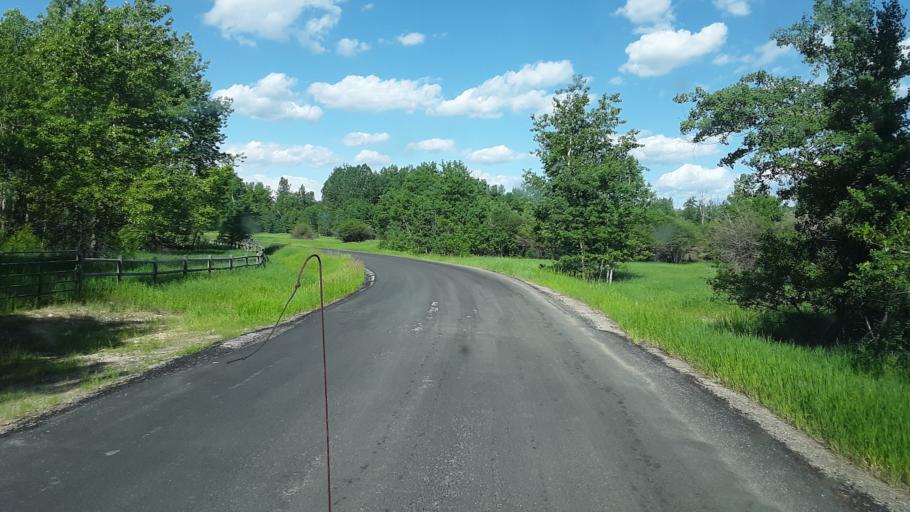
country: US
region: Montana
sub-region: Carbon County
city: Red Lodge
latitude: 45.2773
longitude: -109.2112
